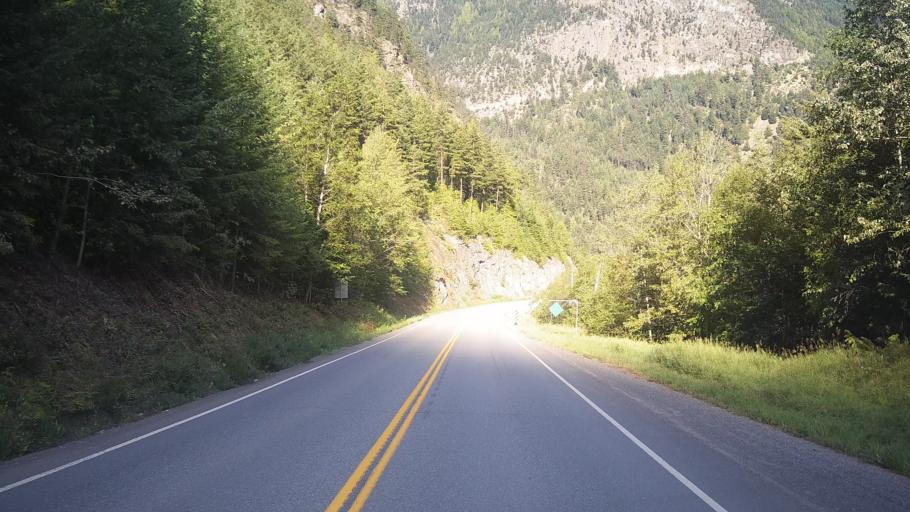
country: CA
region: British Columbia
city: Lillooet
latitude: 50.6382
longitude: -122.0793
